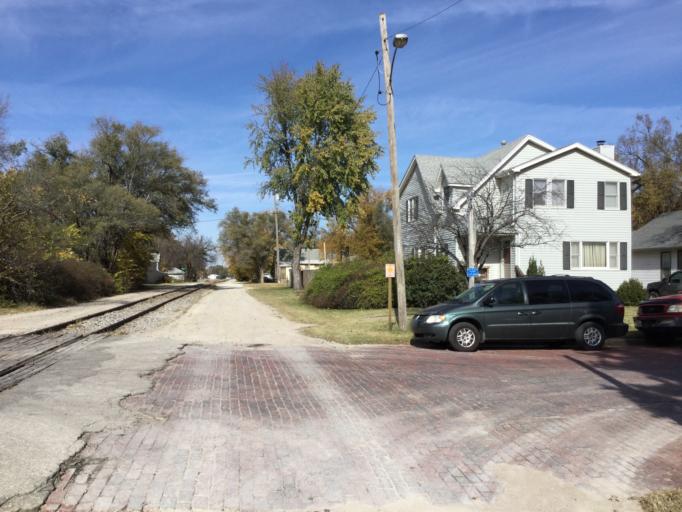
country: US
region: Kansas
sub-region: Harvey County
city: Newton
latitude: 38.0451
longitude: -97.3366
